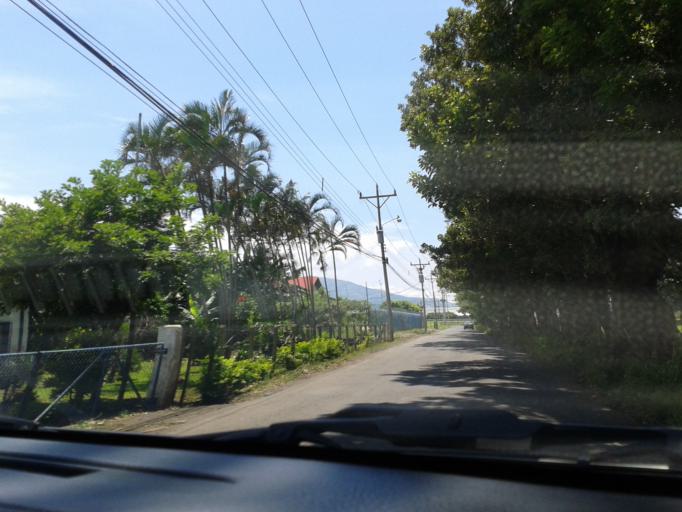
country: CR
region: Alajuela
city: Alajuela
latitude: 9.9972
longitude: -84.2342
